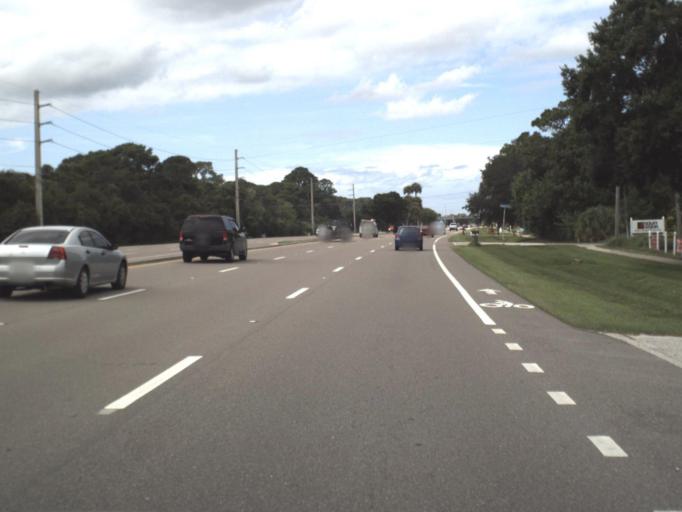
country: US
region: Florida
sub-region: Sarasota County
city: North Sarasota
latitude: 27.3888
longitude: -82.5241
